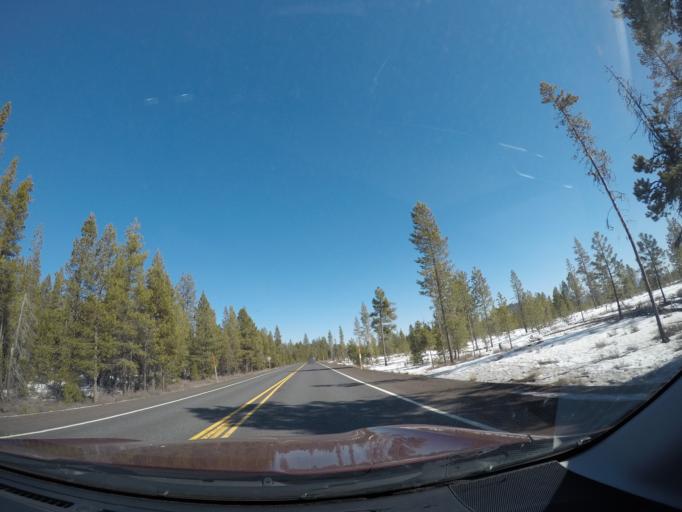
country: US
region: Oregon
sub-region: Deschutes County
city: Three Rivers
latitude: 43.8570
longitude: -121.5187
